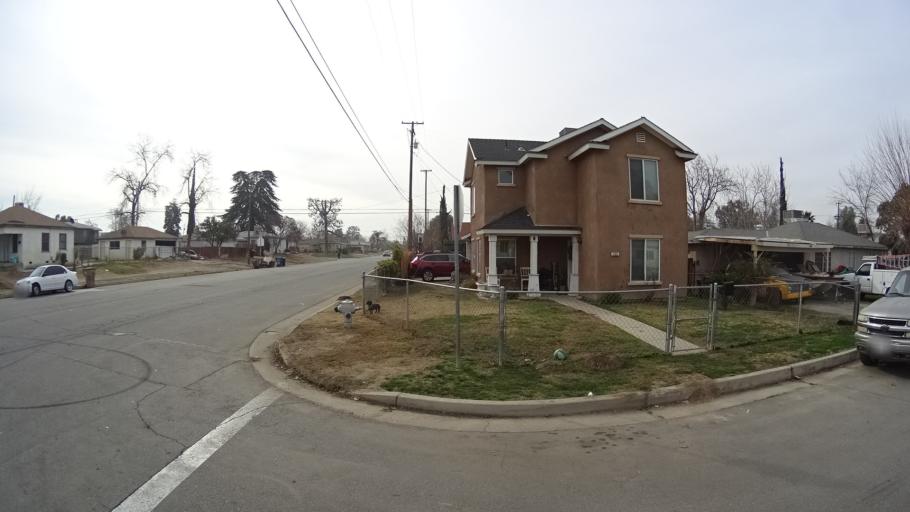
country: US
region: California
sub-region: Kern County
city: Bakersfield
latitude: 35.3598
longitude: -119.0144
